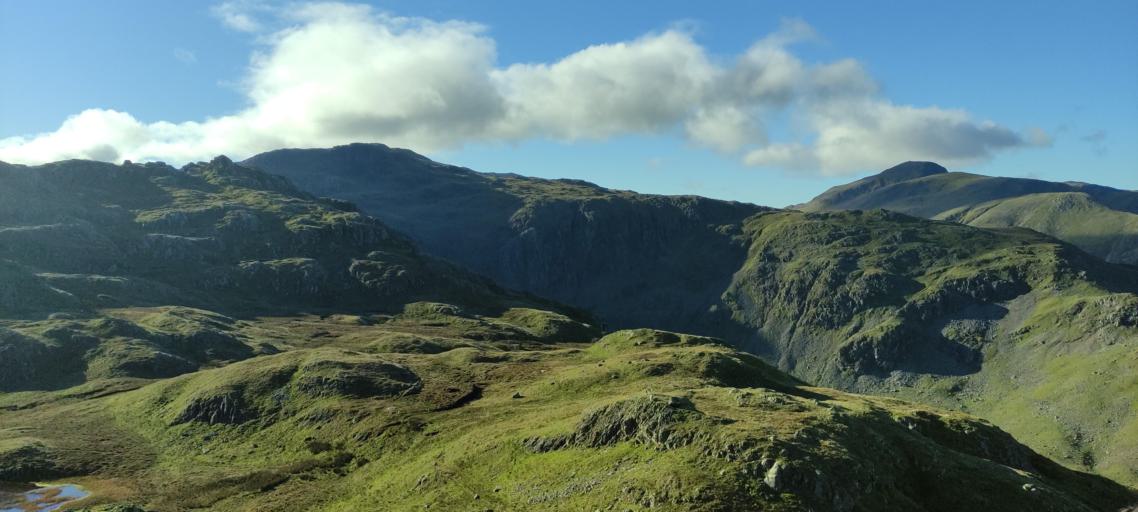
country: GB
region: England
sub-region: Cumbria
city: Keswick
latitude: 54.5022
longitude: -3.1468
